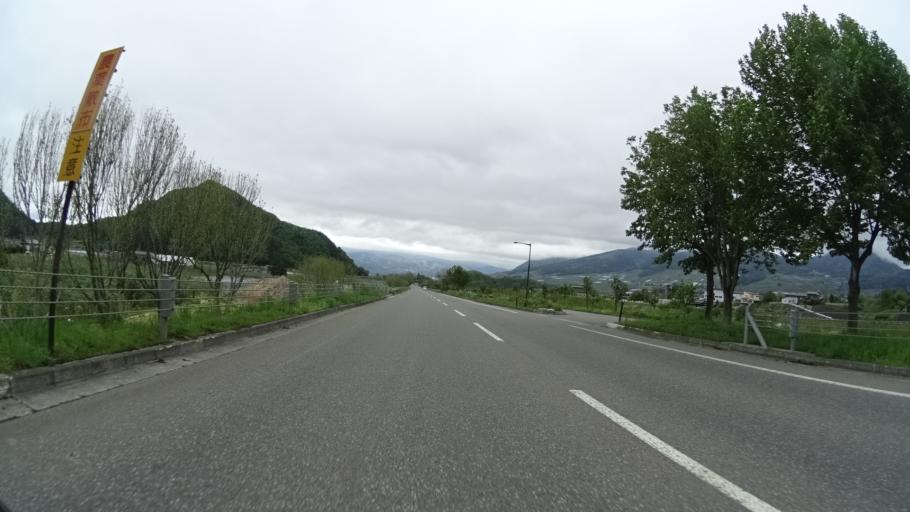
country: JP
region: Nagano
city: Nakano
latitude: 36.7465
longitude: 138.4023
